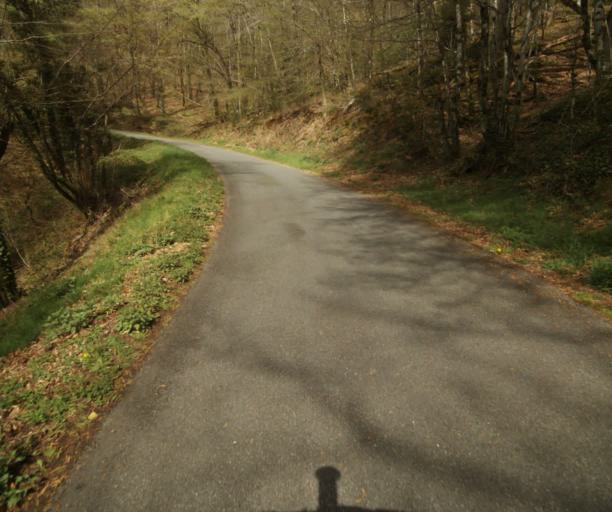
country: FR
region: Limousin
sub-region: Departement de la Correze
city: Laguenne
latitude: 45.2606
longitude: 1.8295
